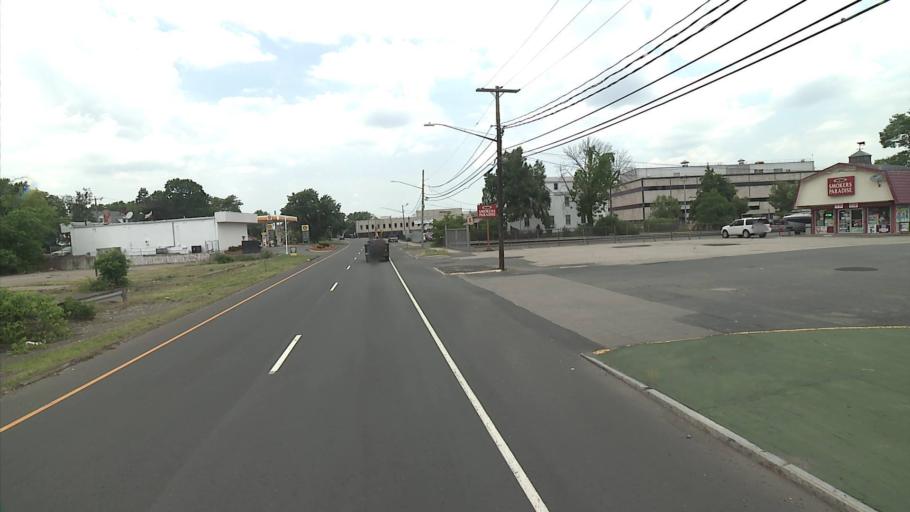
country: US
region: Connecticut
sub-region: Hartford County
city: Wethersfield
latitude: 41.7440
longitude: -72.6334
